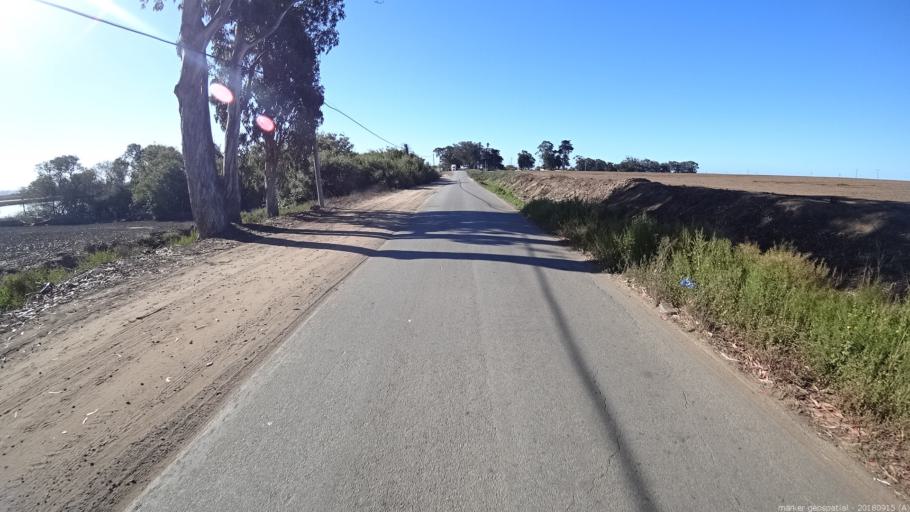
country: US
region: California
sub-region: Monterey County
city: Elkhorn
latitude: 36.8265
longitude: -121.7800
